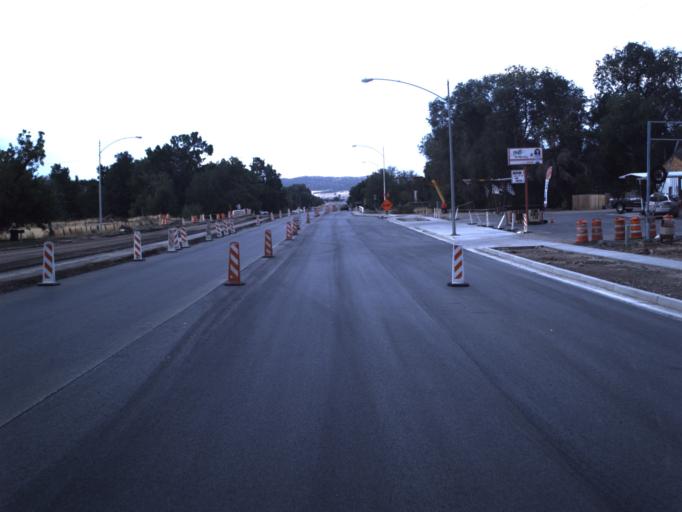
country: US
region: Utah
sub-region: Millard County
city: Fillmore
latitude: 38.9739
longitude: -112.3237
